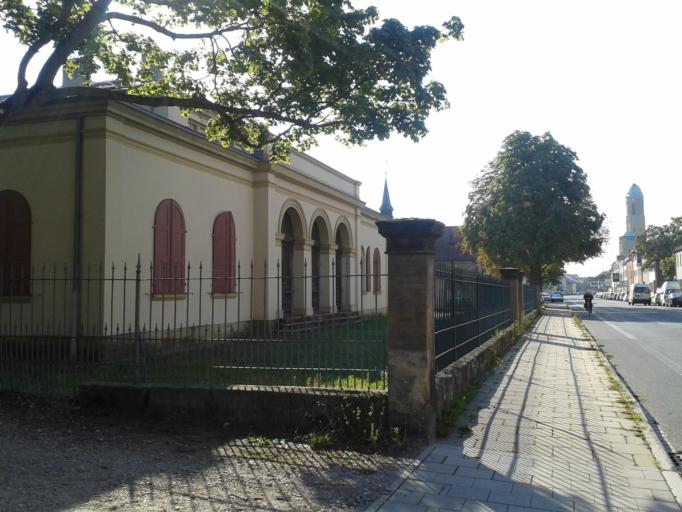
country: DE
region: Bavaria
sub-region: Upper Franconia
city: Bamberg
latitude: 49.9046
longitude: 10.8866
